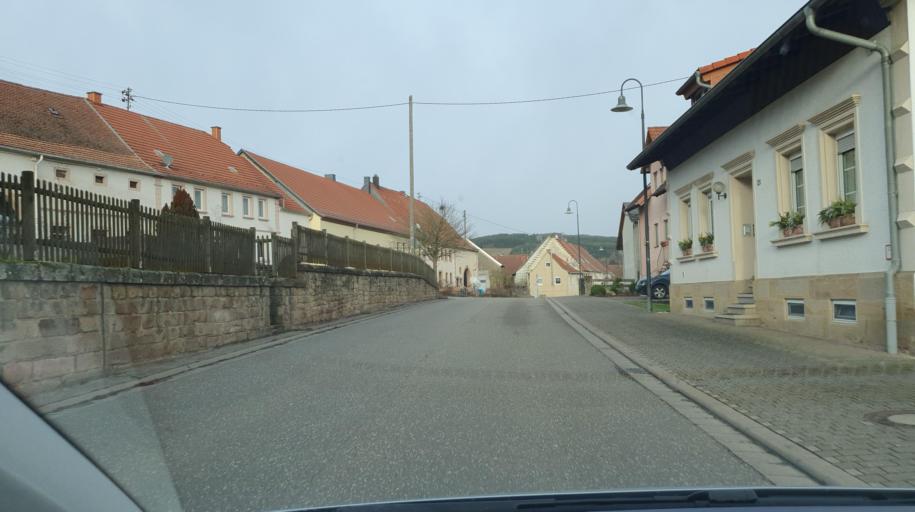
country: DE
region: Rheinland-Pfalz
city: Rathsweiler
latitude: 49.5973
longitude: 7.4575
